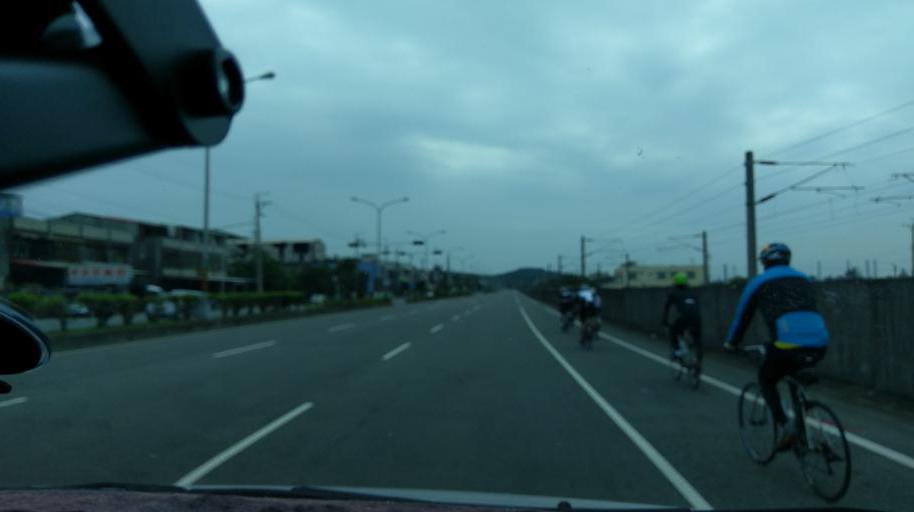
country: TW
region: Taiwan
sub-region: Miaoli
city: Miaoli
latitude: 24.5164
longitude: 120.6915
